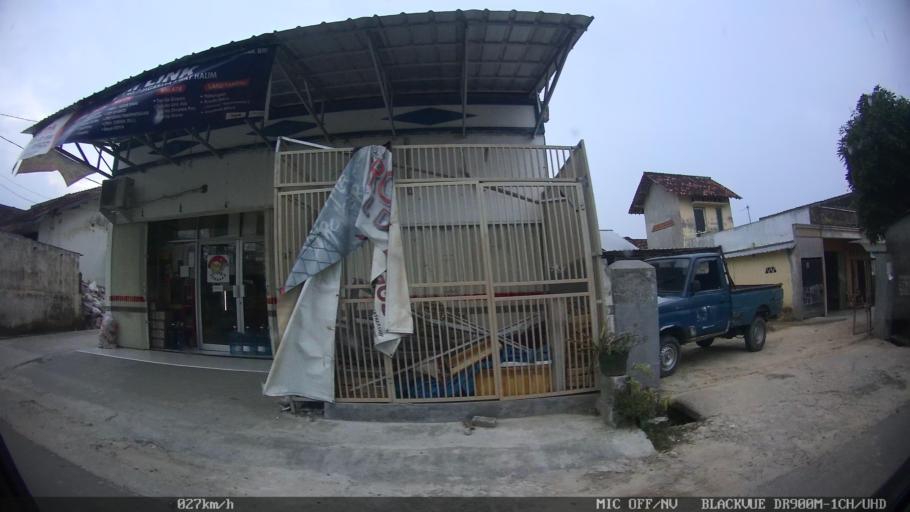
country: ID
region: Lampung
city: Kedaton
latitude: -5.3990
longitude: 105.2656
